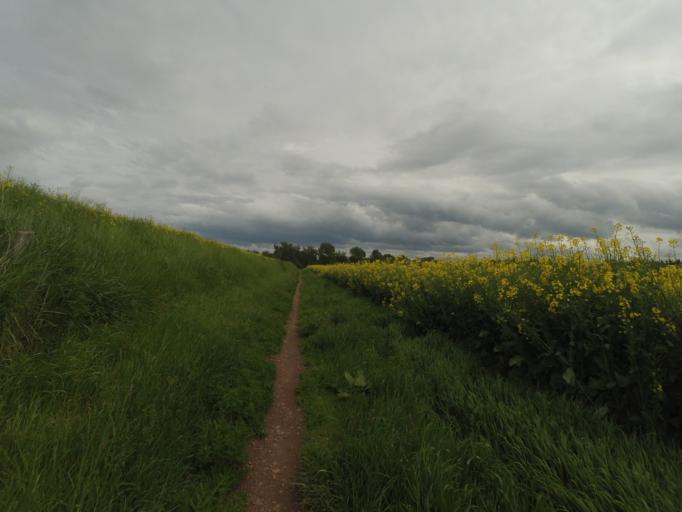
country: GB
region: Scotland
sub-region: East Lothian
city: Ormiston
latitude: 55.9137
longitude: -2.9275
